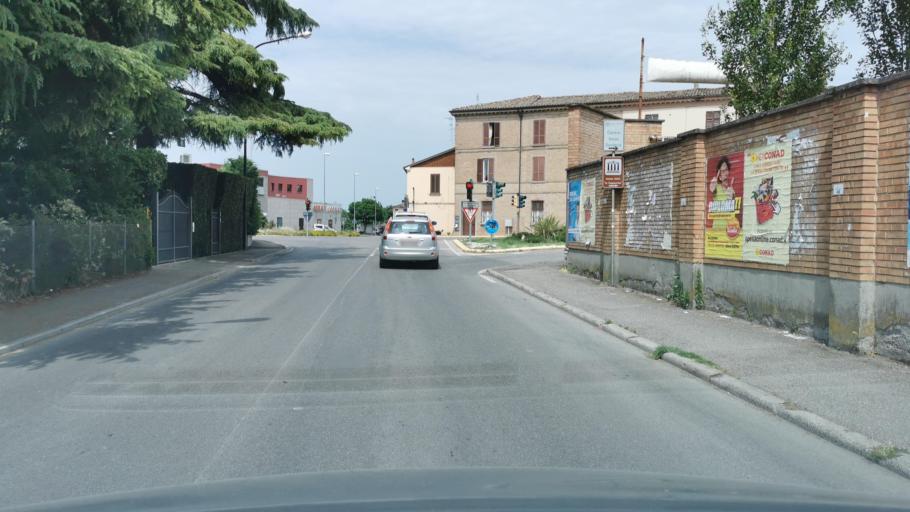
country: IT
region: Emilia-Romagna
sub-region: Provincia di Ravenna
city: Bagnacavallo
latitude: 44.4185
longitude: 11.9736
